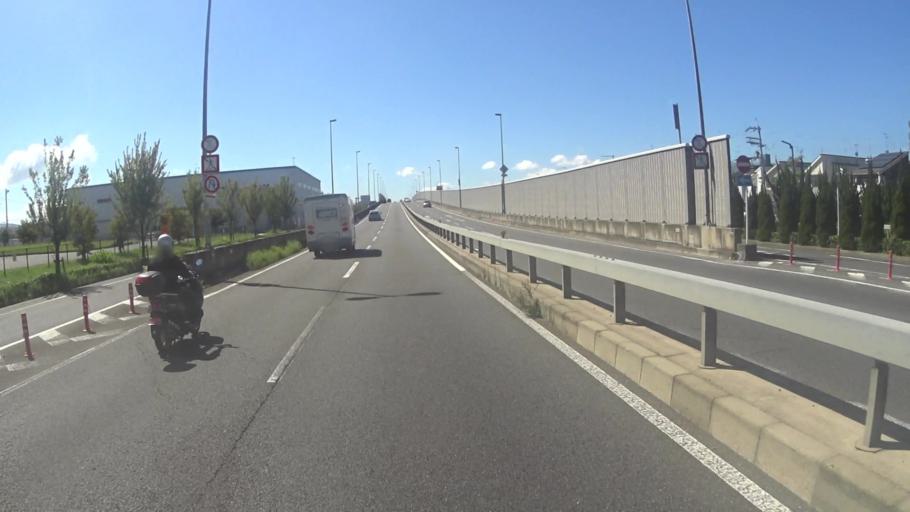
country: JP
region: Kyoto
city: Uji
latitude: 34.8780
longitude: 135.7624
